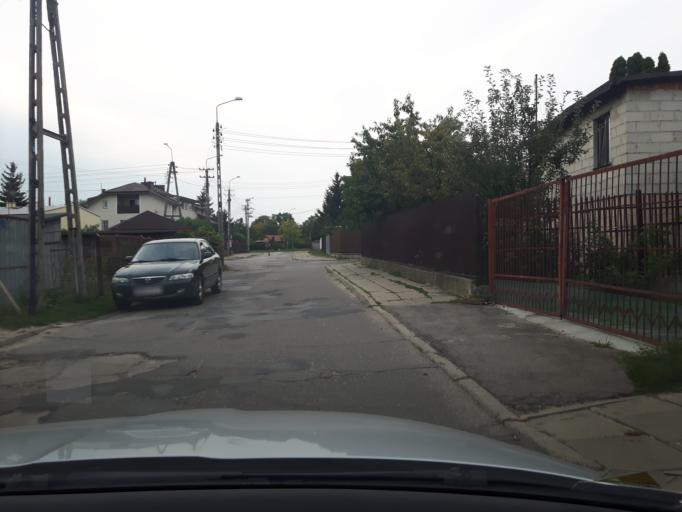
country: PL
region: Masovian Voivodeship
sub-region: Powiat wolominski
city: Zabki
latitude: 52.2904
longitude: 21.1002
